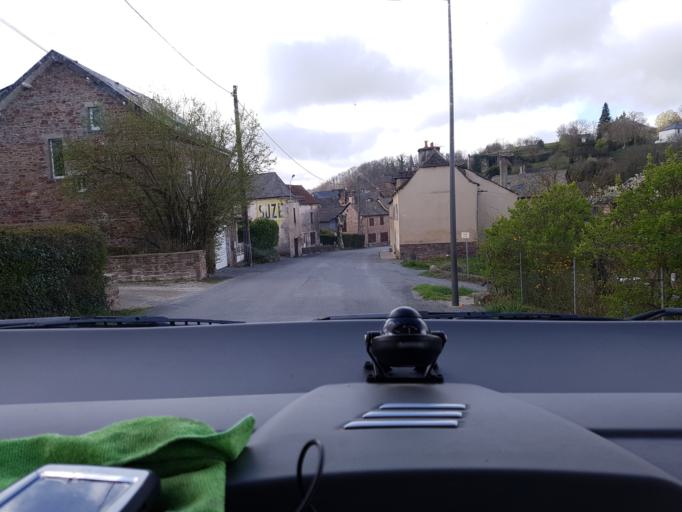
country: FR
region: Midi-Pyrenees
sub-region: Departement de l'Aveyron
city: Moyrazes
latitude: 44.3778
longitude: 2.4451
